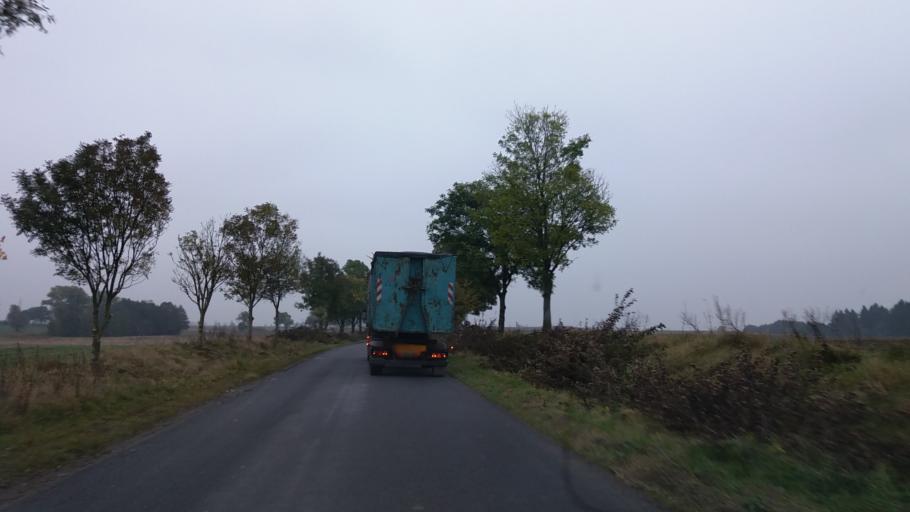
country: PL
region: West Pomeranian Voivodeship
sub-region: Powiat choszczenski
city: Bierzwnik
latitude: 53.0452
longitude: 15.6773
